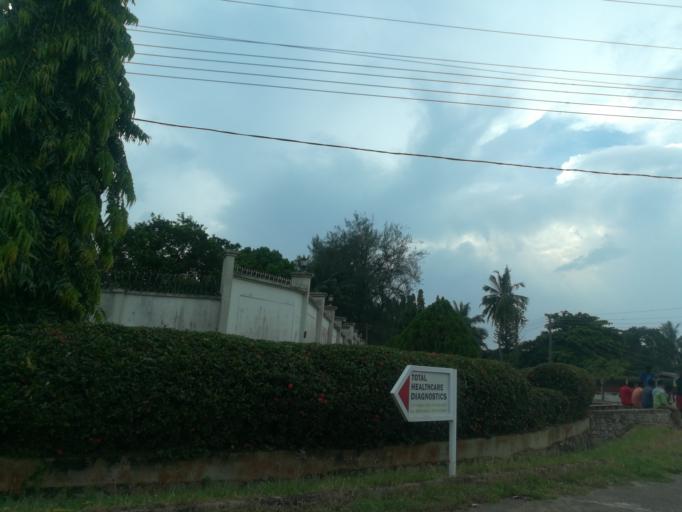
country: NG
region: Oyo
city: Ibadan
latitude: 7.4208
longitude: 3.9065
